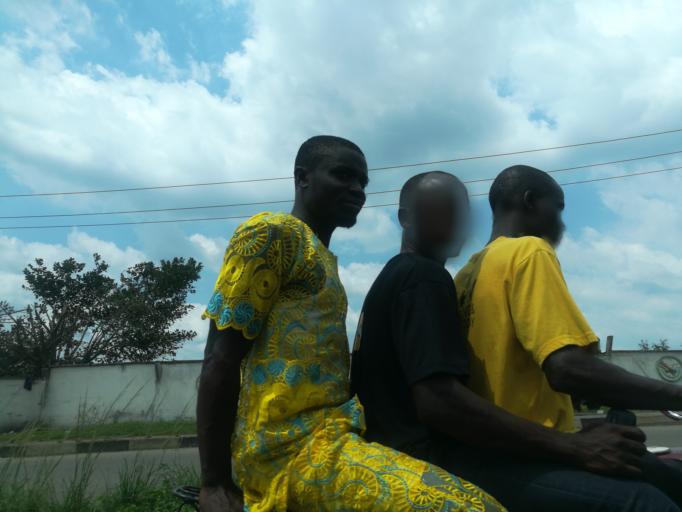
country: NG
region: Oyo
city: Ibadan
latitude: 7.3988
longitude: 3.8828
